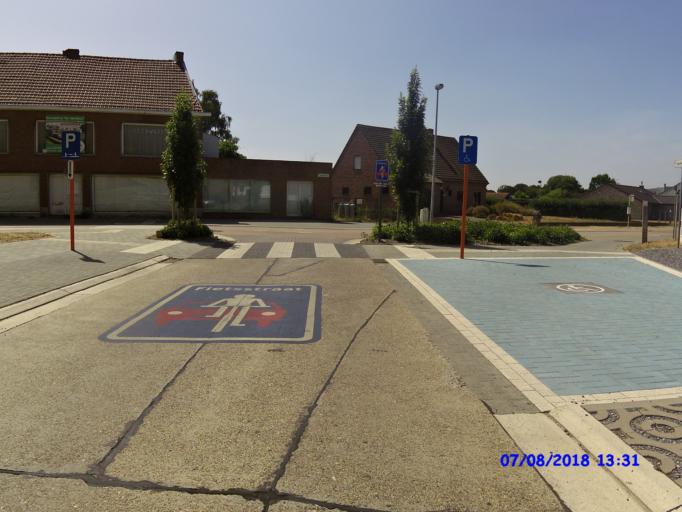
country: BE
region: Flanders
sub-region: Provincie Antwerpen
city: Laakdal
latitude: 51.0664
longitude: 4.9849
